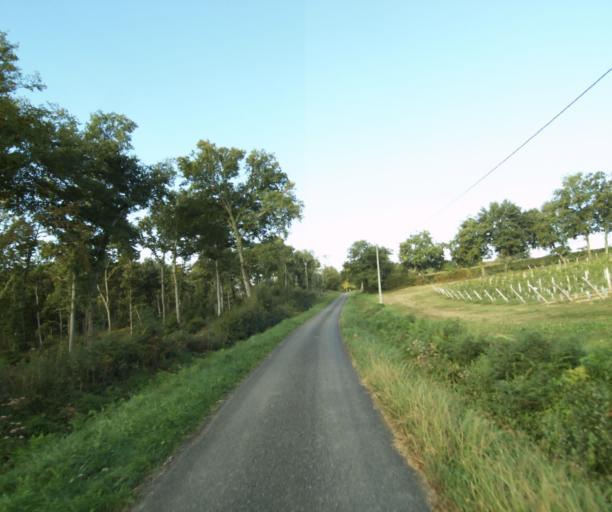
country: FR
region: Midi-Pyrenees
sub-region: Departement du Gers
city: Eauze
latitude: 43.8986
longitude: 0.0216
